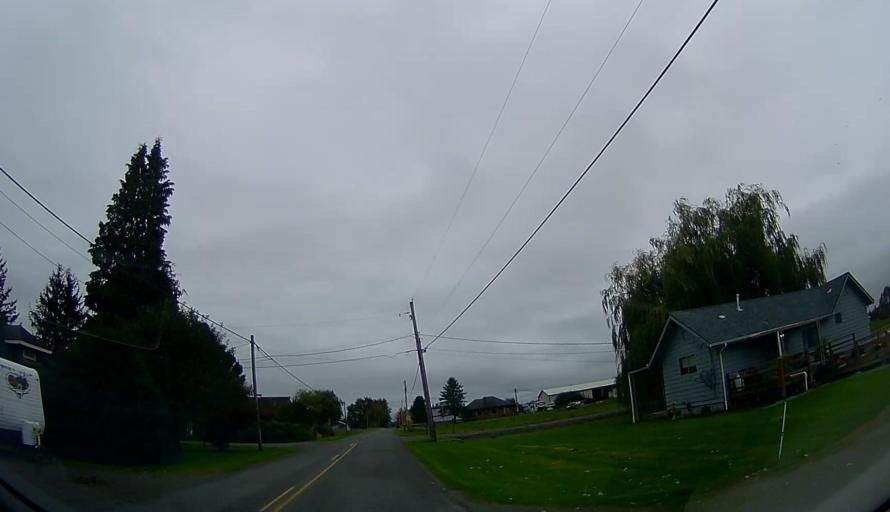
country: US
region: Washington
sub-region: Skagit County
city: Sedro-Woolley
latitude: 48.5143
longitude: -122.1717
